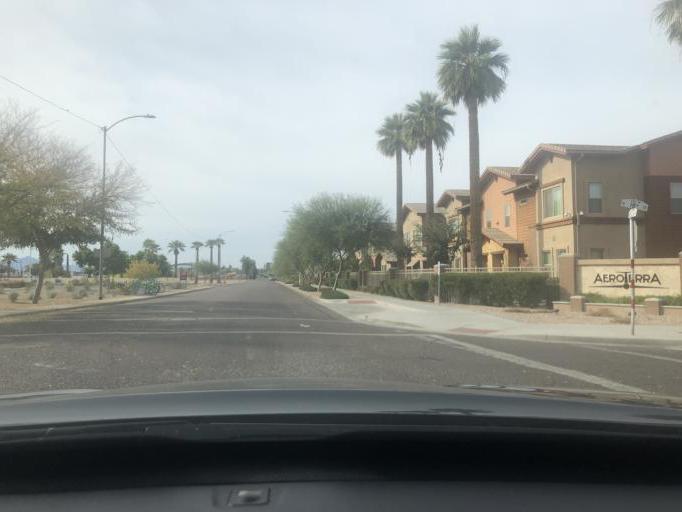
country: US
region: Arizona
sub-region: Maricopa County
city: Phoenix
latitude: 33.4559
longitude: -112.0432
